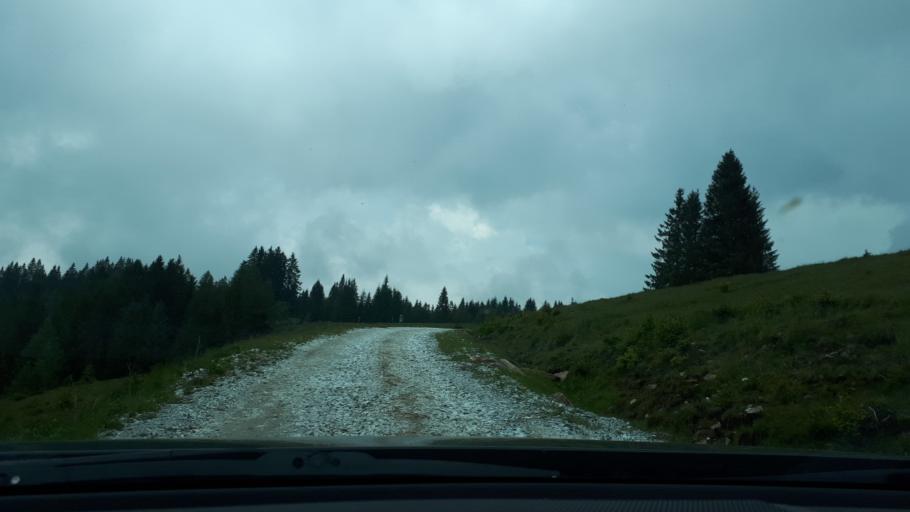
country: AT
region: Styria
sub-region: Politischer Bezirk Voitsberg
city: Modriach
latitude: 46.9122
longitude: 15.0496
